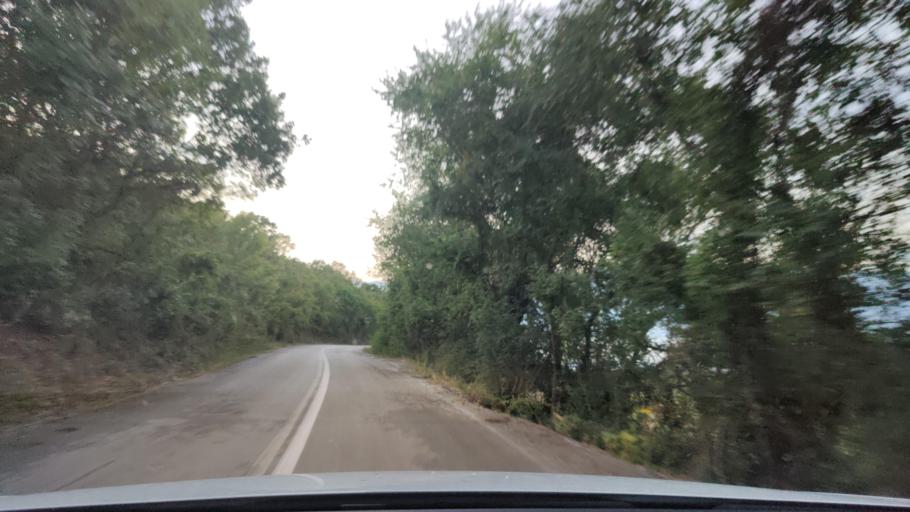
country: GR
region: Central Macedonia
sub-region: Nomos Serron
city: Chrysochorafa
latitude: 41.1653
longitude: 23.1819
